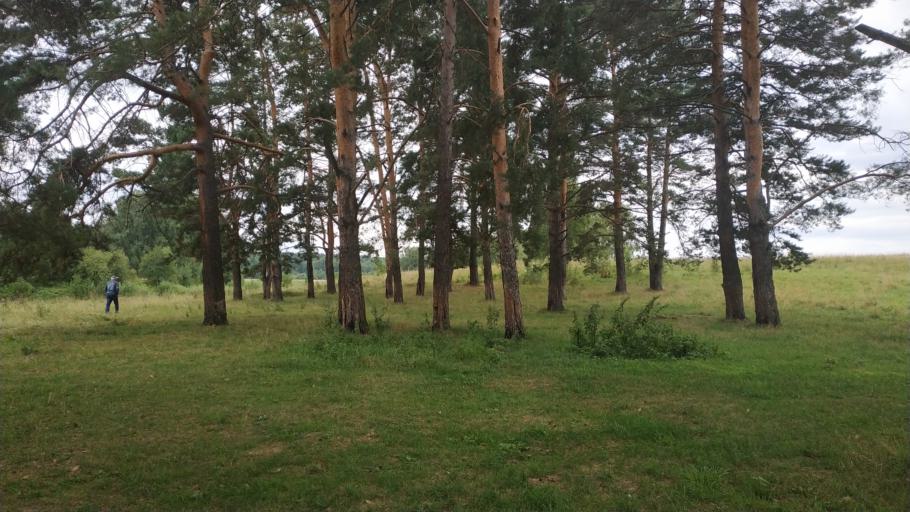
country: RU
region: Sverdlovsk
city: Alapayevsk
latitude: 57.7320
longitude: 61.9710
